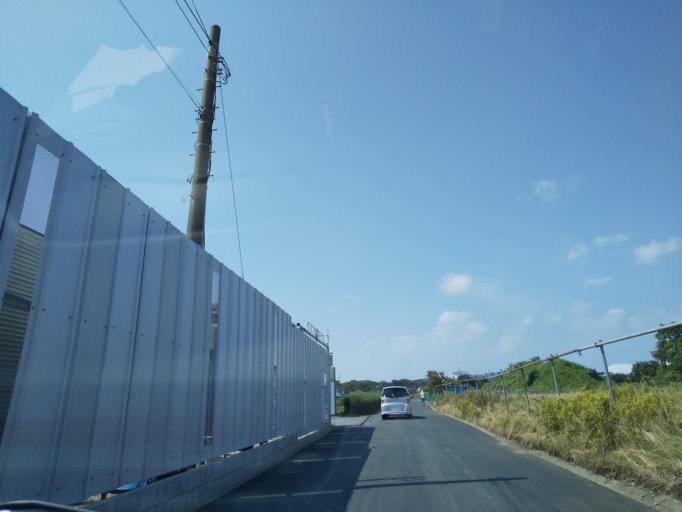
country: JP
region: Kanagawa
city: Zama
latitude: 35.5213
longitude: 139.3891
